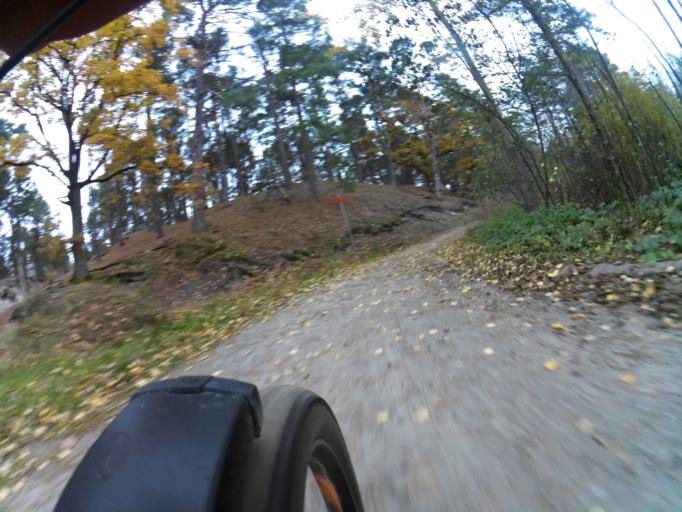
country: PL
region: Pomeranian Voivodeship
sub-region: Powiat wejherowski
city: Choczewo
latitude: 54.7829
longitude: 17.7411
